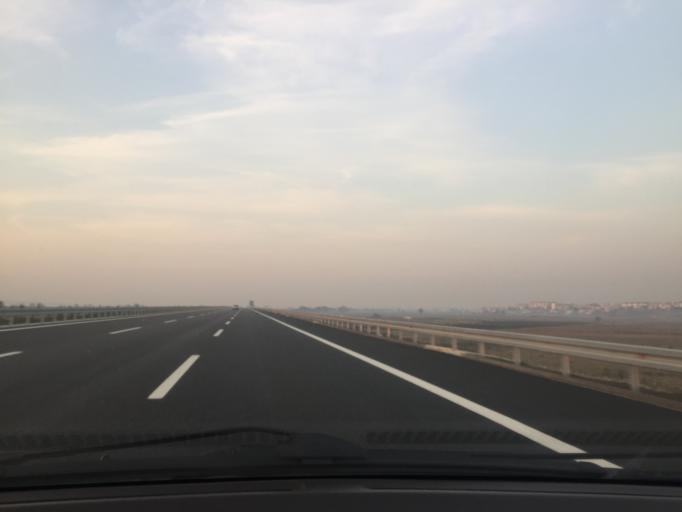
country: TR
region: Bursa
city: Karacabey
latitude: 40.2092
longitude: 28.3848
